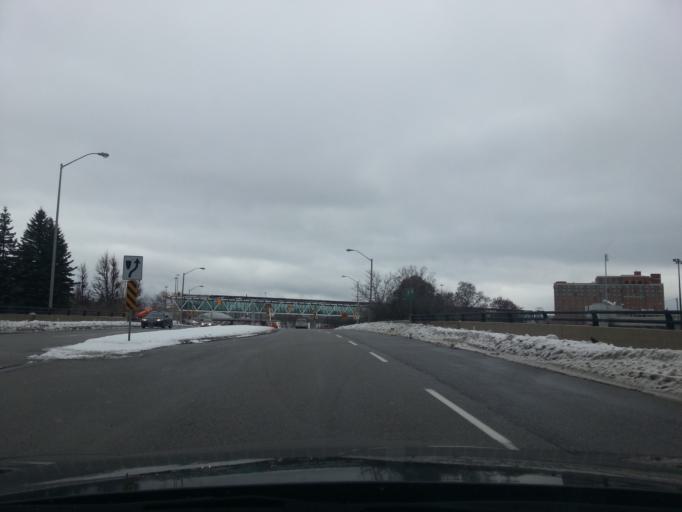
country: CA
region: Ontario
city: Ottawa
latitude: 45.4184
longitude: -75.6503
